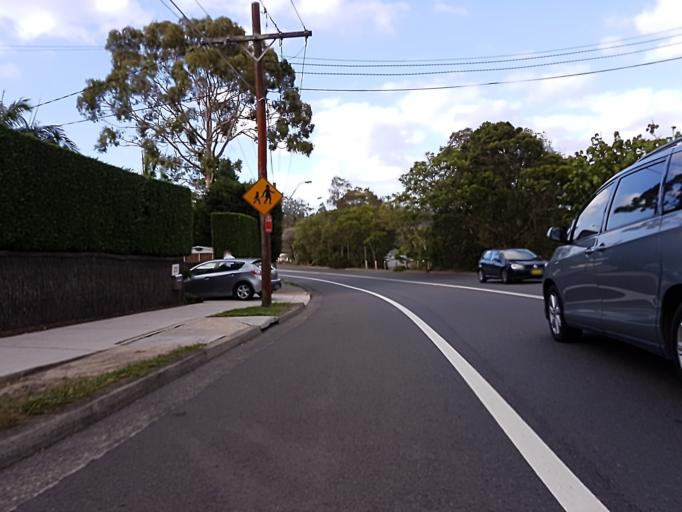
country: AU
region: New South Wales
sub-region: Manly Vale
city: Balgowlah
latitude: -33.7904
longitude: 151.2413
